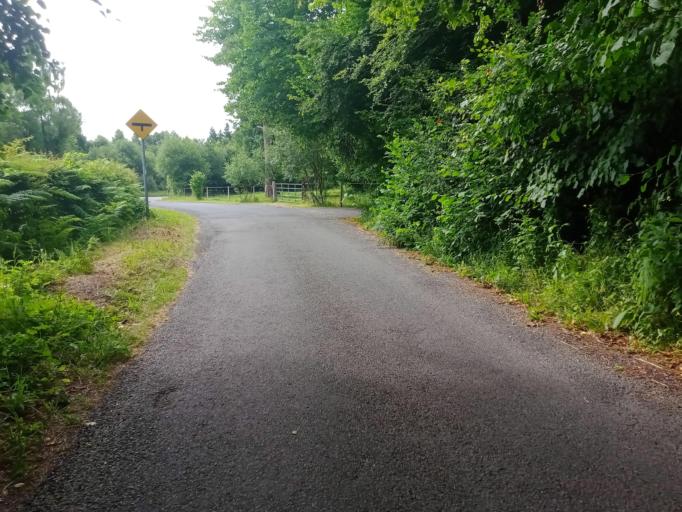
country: IE
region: Leinster
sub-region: Laois
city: Abbeyleix
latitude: 52.8975
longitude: -7.3605
